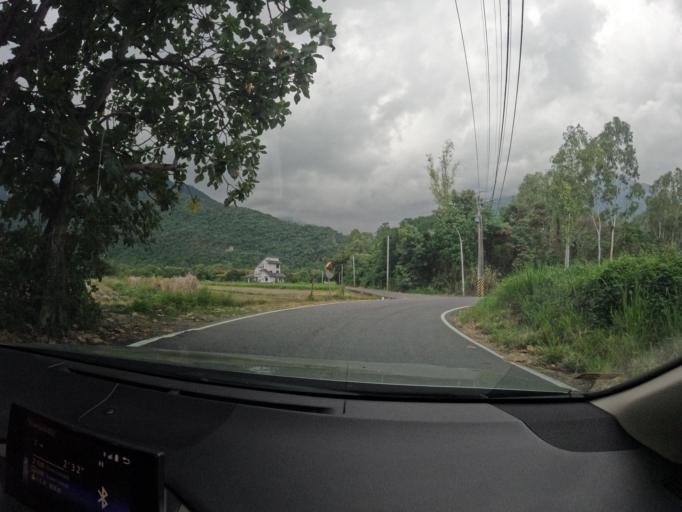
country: TW
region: Taiwan
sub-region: Hualien
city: Hualian
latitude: 24.0941
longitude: 121.6176
